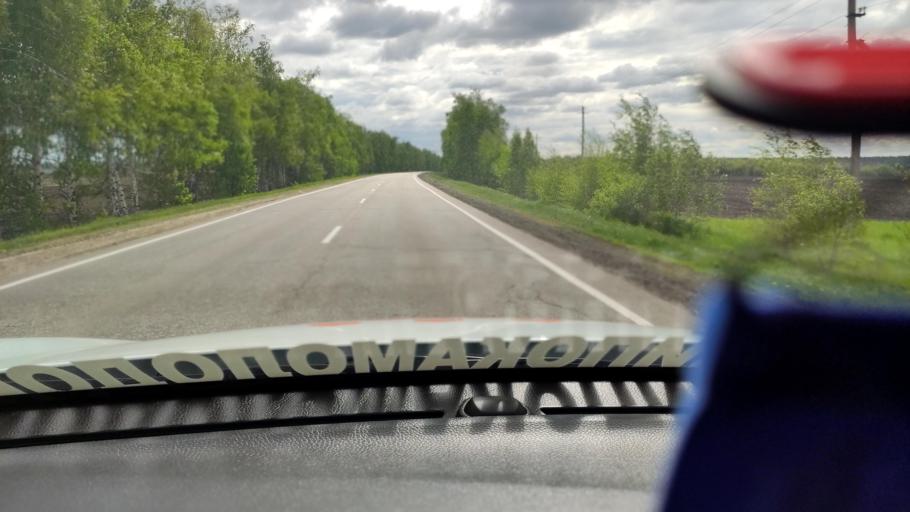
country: RU
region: Voronezj
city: Liski
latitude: 50.7973
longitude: 39.3596
